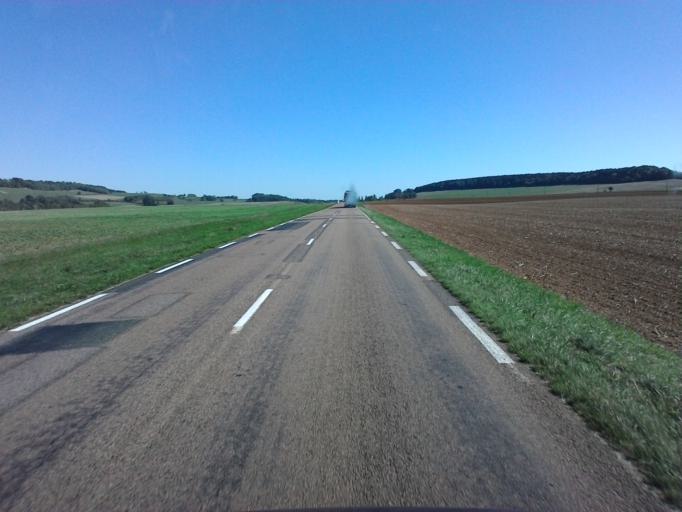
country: FR
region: Champagne-Ardenne
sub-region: Departement de la Haute-Marne
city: Chateauvillain
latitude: 48.0861
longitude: 5.0044
